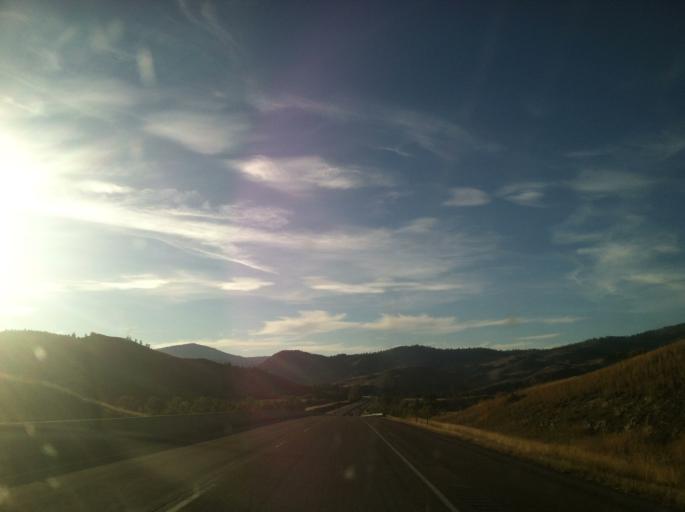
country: US
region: Montana
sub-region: Granite County
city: Philipsburg
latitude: 46.7048
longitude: -113.2505
